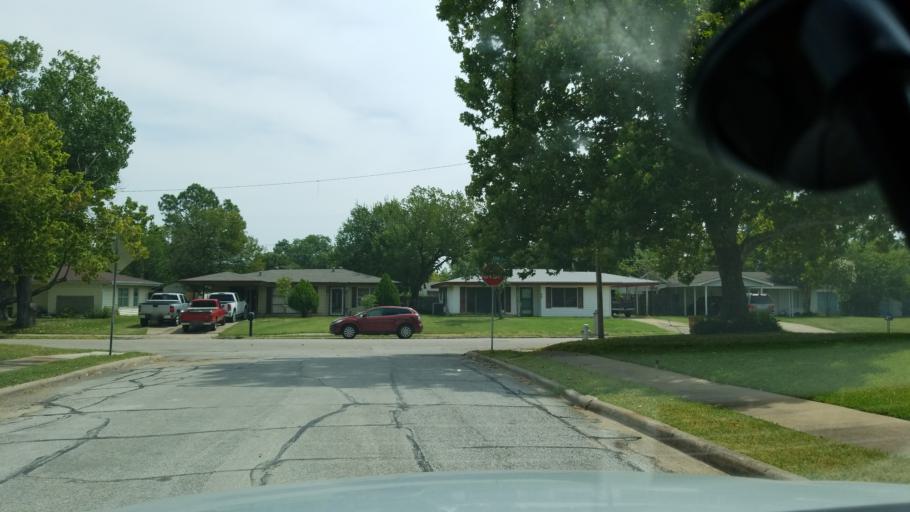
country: US
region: Texas
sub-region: Dallas County
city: Irving
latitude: 32.8299
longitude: -96.9880
